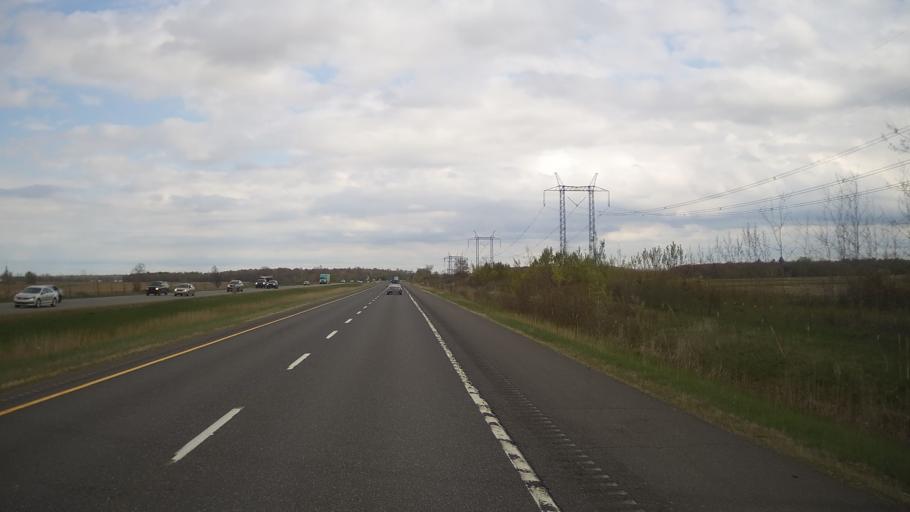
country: CA
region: Quebec
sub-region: Monteregie
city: Saint-Cesaire
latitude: 45.3761
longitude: -72.9817
